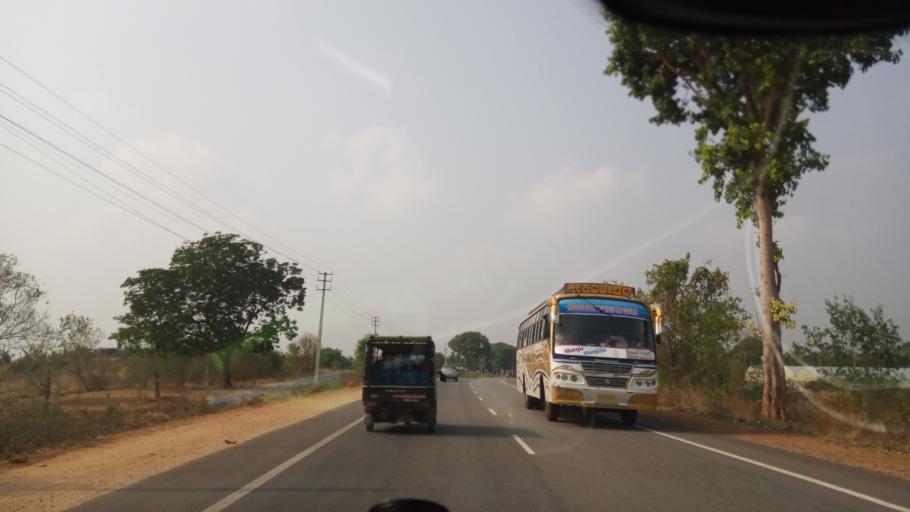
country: IN
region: Karnataka
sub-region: Mandya
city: Nagamangala
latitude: 12.7939
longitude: 76.7512
